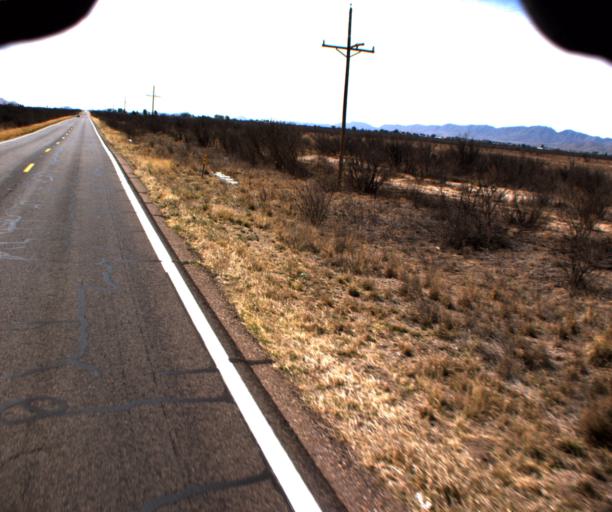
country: US
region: Arizona
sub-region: Cochise County
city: Willcox
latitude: 32.0220
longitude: -109.8720
